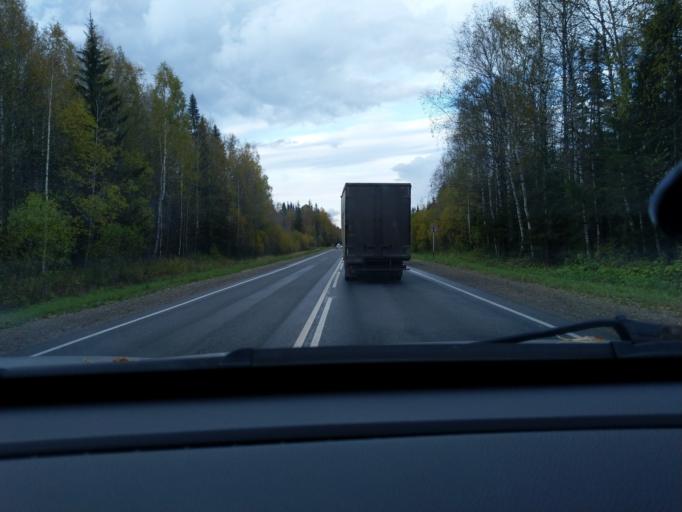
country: RU
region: Perm
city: Dobryanka
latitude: 58.4064
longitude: 56.5135
